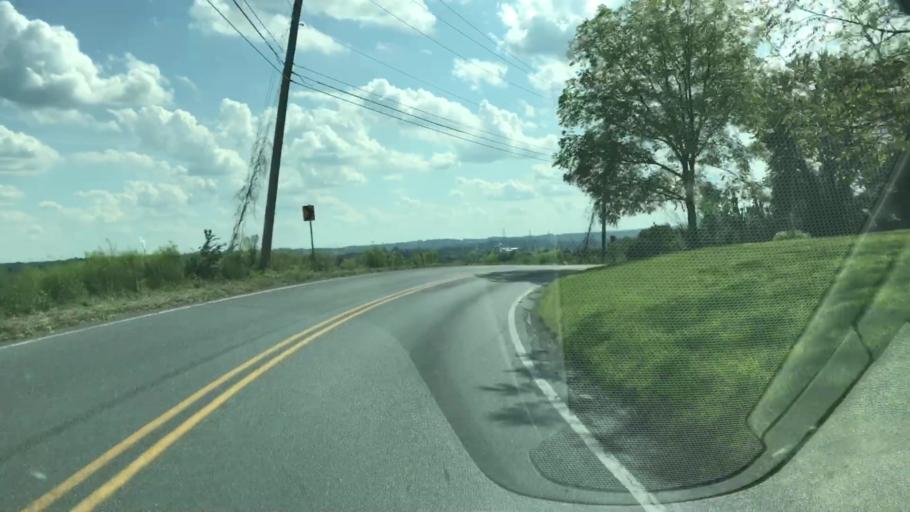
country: US
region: Pennsylvania
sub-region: Dauphin County
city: Middletown
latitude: 40.1830
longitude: -76.6940
